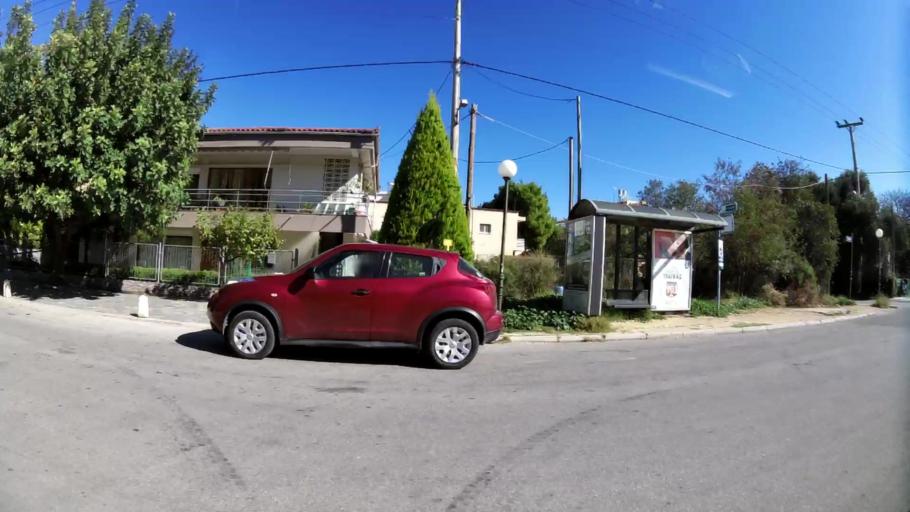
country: GR
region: Attica
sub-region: Nomarchia Athinas
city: Nea Erythraia
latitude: 38.0961
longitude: 23.7928
